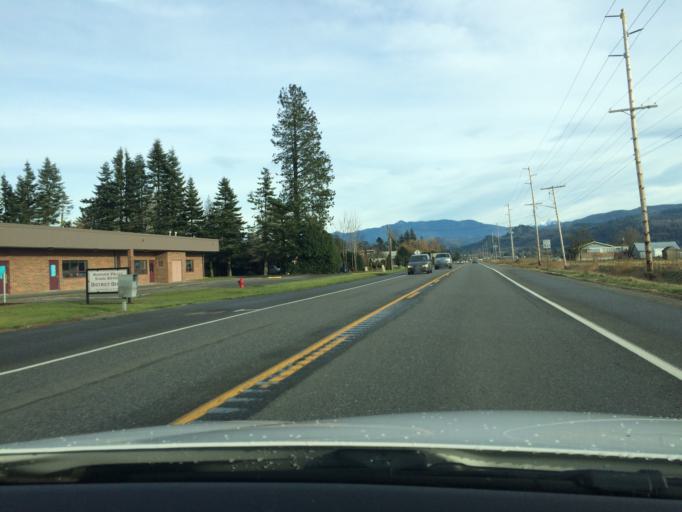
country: US
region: Washington
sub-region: Whatcom County
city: Nooksack
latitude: 48.9638
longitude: -122.3078
